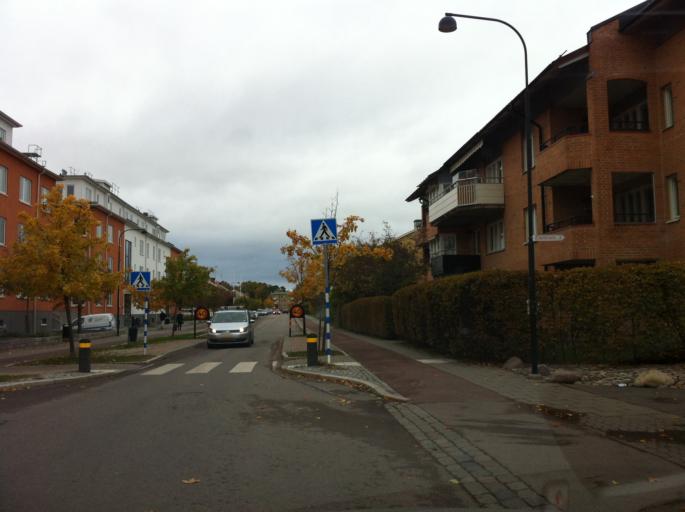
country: SE
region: OEstergoetland
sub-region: Linkopings Kommun
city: Linkoping
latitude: 58.4046
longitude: 15.6008
